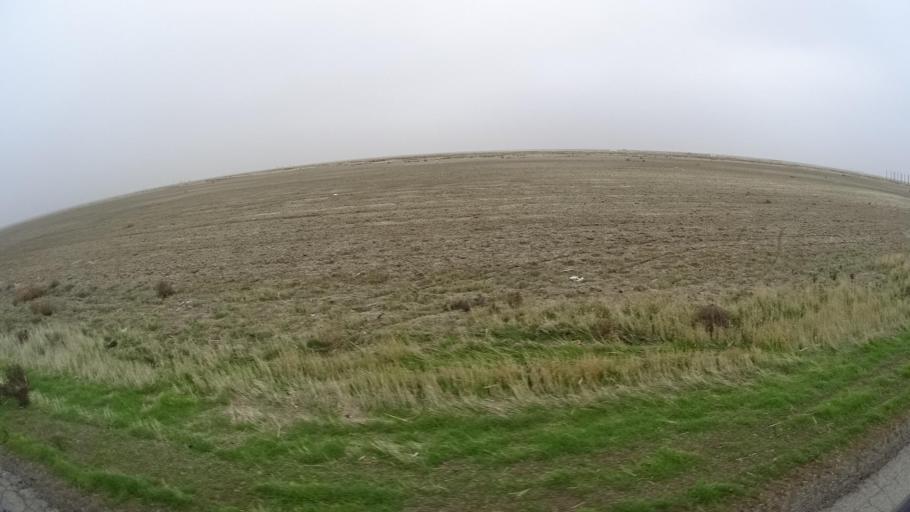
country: US
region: California
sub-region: Tulare County
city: Alpaugh
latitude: 35.7174
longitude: -119.4702
